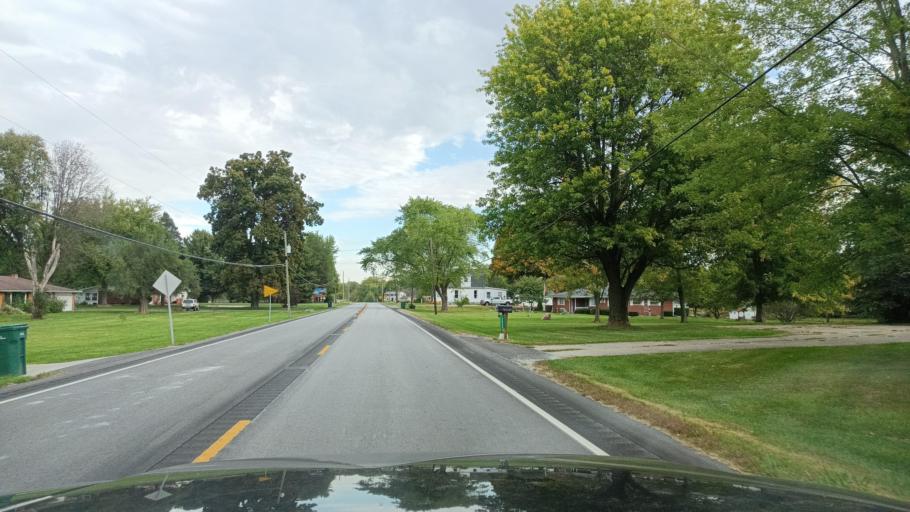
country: US
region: Indiana
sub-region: Delaware County
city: Daleville
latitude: 40.1372
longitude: -85.5438
